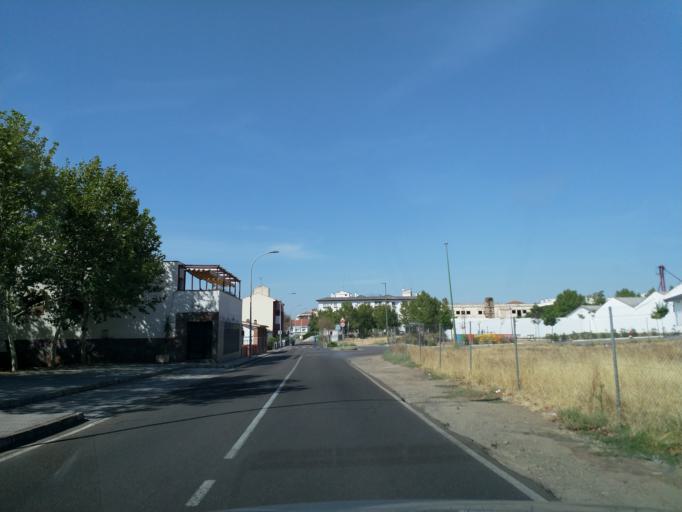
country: ES
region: Extremadura
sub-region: Provincia de Badajoz
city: Merida
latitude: 38.9253
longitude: -6.3456
